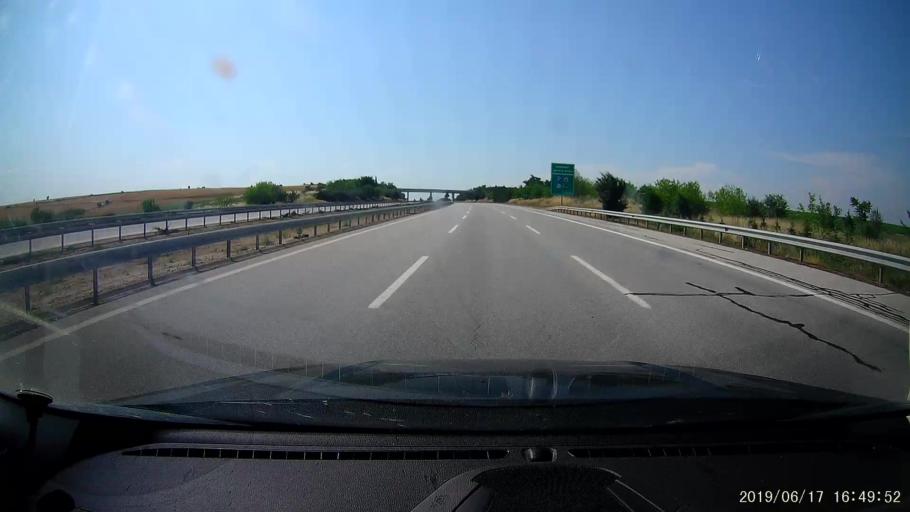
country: TR
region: Kirklareli
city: Babaeski
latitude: 41.5161
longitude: 27.1041
